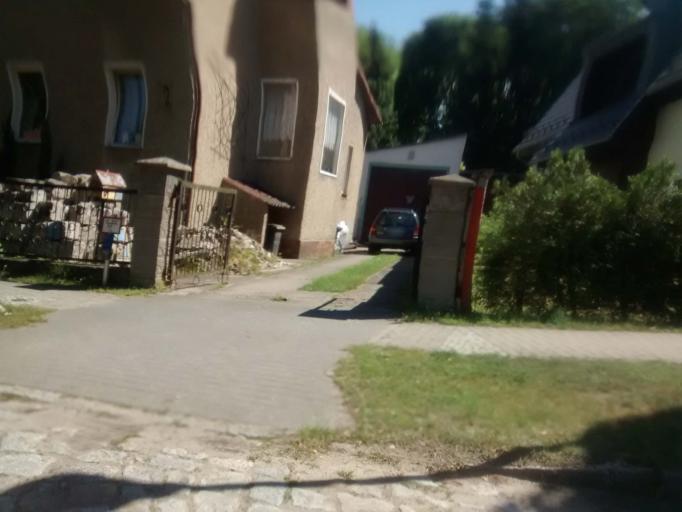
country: DE
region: Brandenburg
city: Hohen Neuendorf
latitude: 52.6758
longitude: 13.2710
